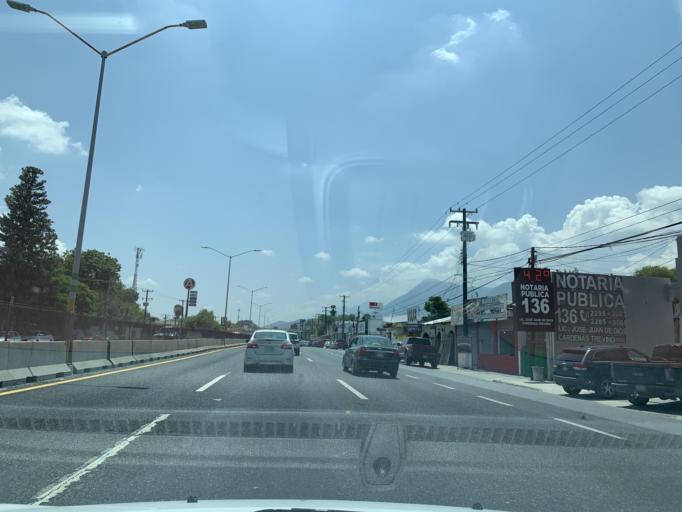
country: MX
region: Nuevo Leon
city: Santiago
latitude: 25.4072
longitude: -100.1350
